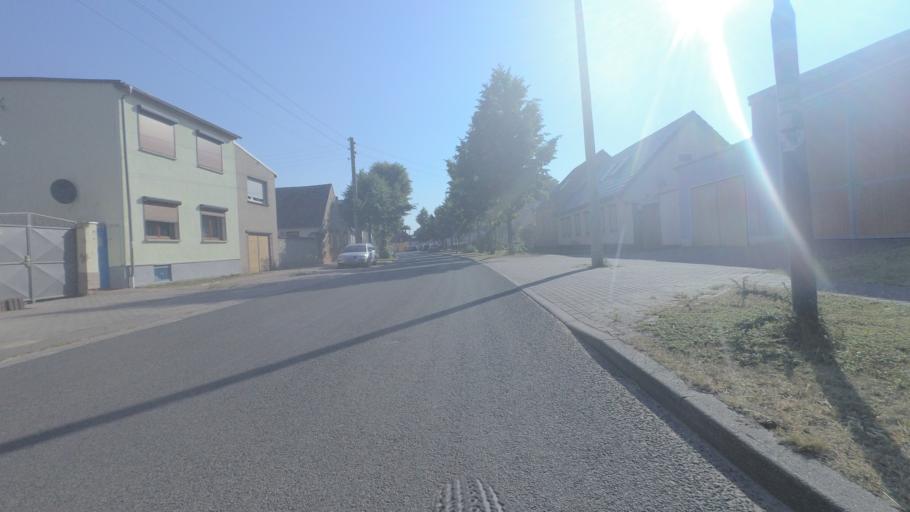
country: DE
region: Saxony-Anhalt
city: Osternienburg
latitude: 51.7924
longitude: 12.0269
